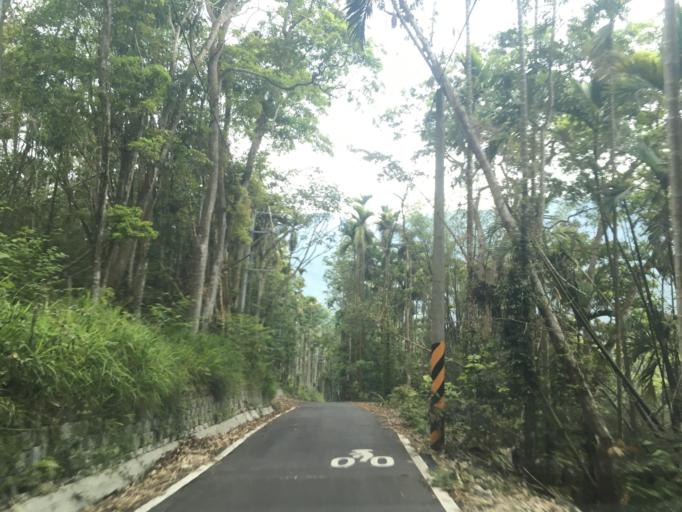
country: TW
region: Taiwan
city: Zhongxing New Village
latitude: 24.0463
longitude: 120.7996
